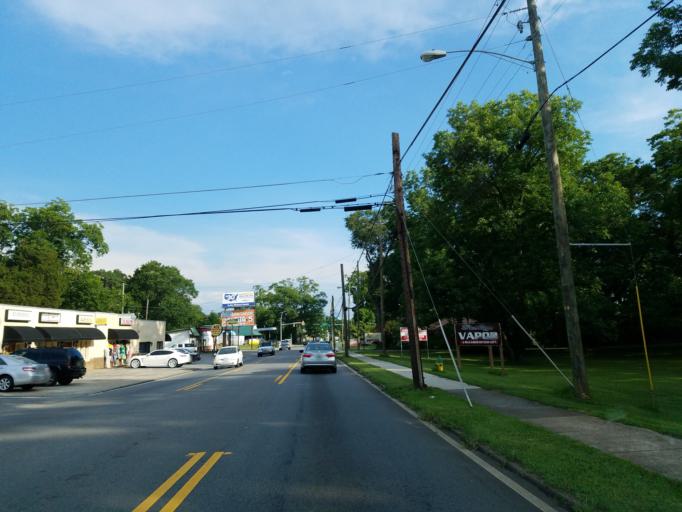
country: US
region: Georgia
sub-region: Bartow County
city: Cartersville
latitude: 34.1802
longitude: -84.7938
